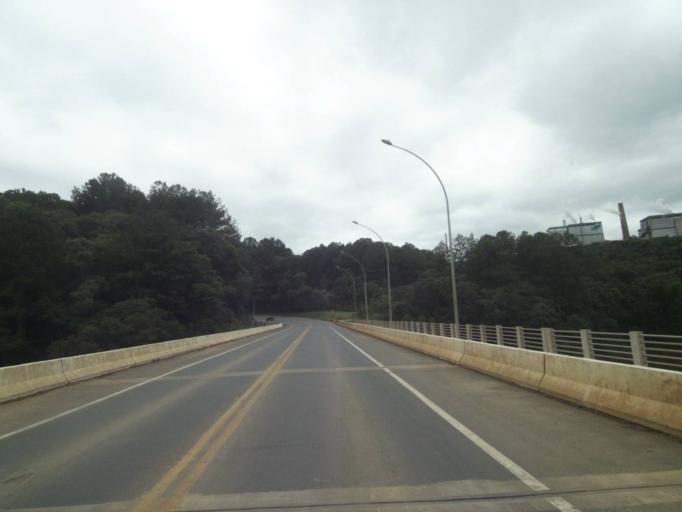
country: BR
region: Parana
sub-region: Telemaco Borba
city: Telemaco Borba
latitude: -24.3126
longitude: -50.6154
